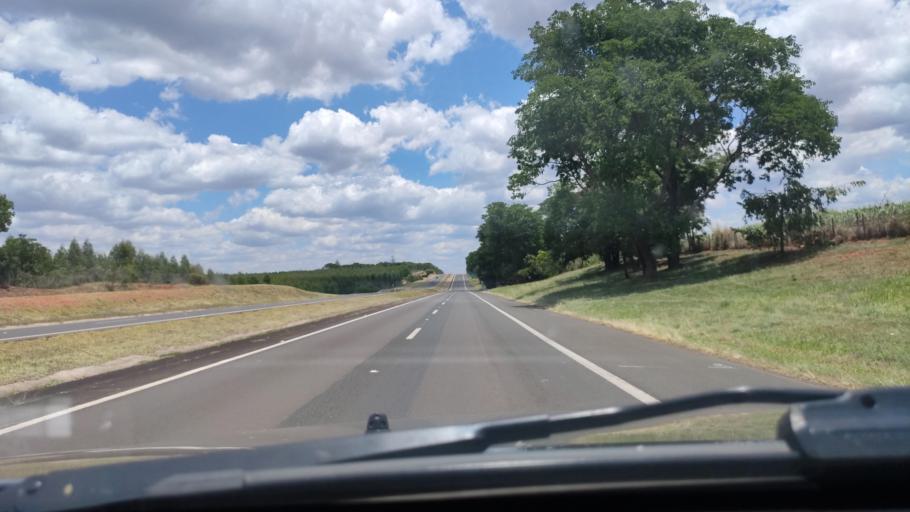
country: BR
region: Sao Paulo
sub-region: Duartina
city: Duartina
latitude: -22.5053
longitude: -49.2873
